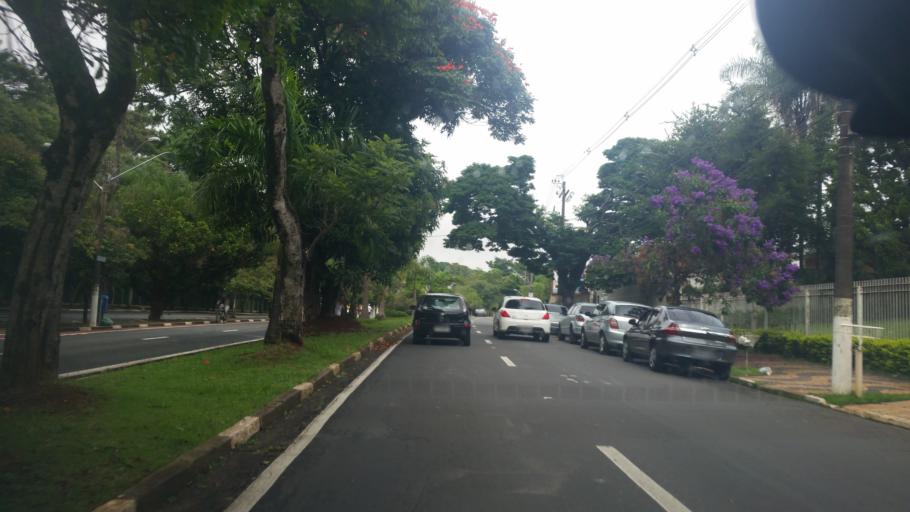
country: BR
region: Sao Paulo
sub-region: Campinas
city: Campinas
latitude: -22.8733
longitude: -47.0526
